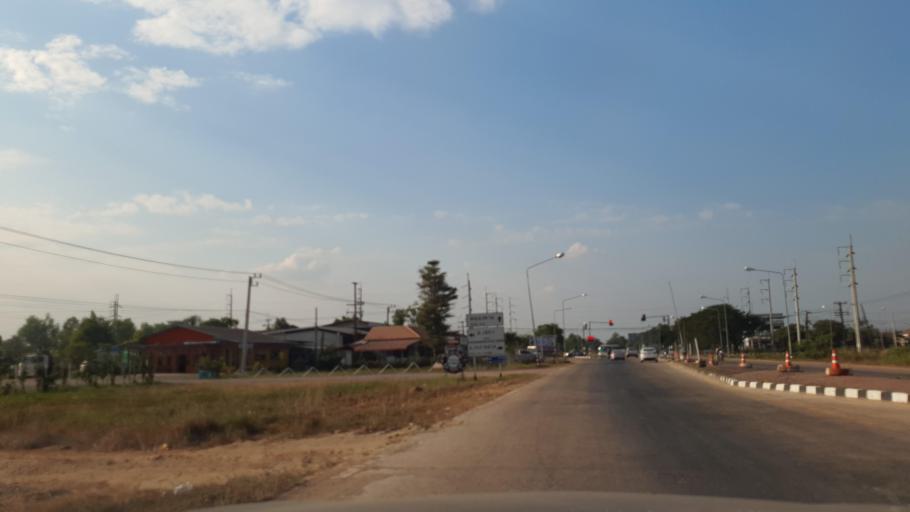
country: TH
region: Nakhon Phanom
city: Ban Phaeng
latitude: 18.0297
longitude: 104.1415
